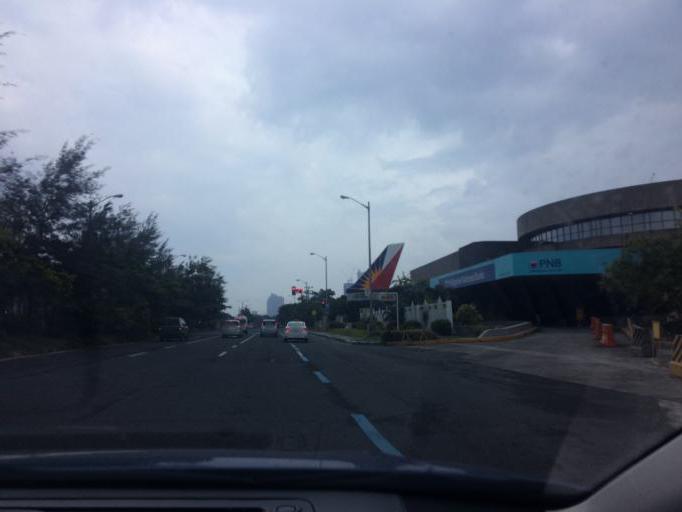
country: PH
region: Metro Manila
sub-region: City of Manila
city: Port Area
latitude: 14.5476
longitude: 120.9870
